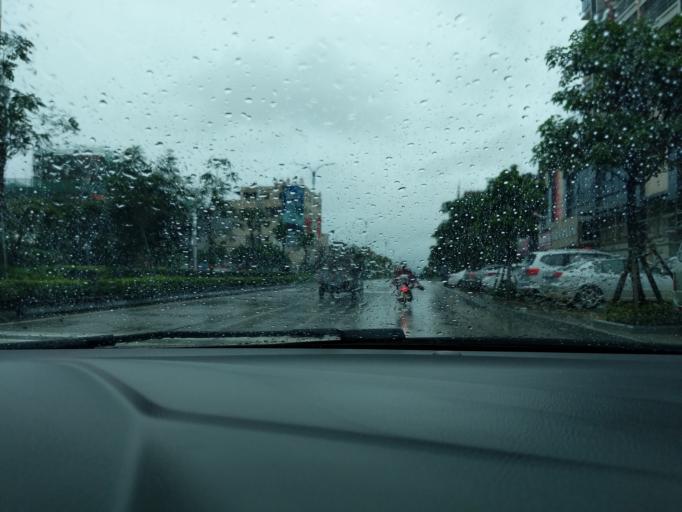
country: CN
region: Guangdong
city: Pingshi
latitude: 22.2036
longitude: 112.3265
